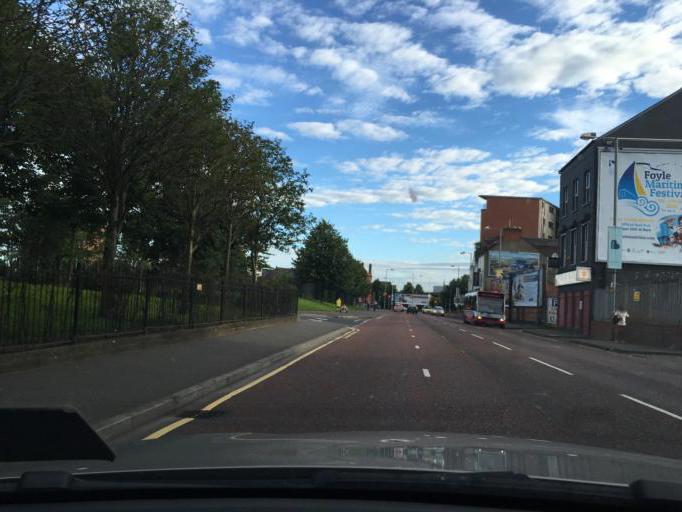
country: GB
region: Northern Ireland
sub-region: City of Belfast
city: Belfast
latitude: 54.5934
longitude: -5.9249
